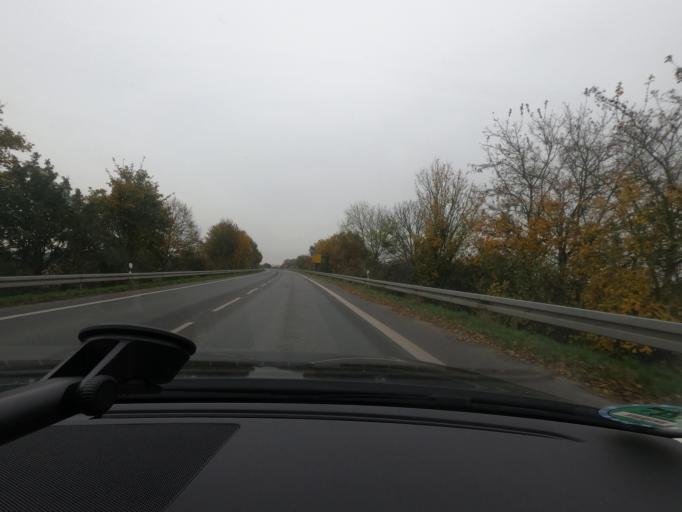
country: DE
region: North Rhine-Westphalia
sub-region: Regierungsbezirk Dusseldorf
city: Uedem
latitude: 51.6294
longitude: 6.2856
